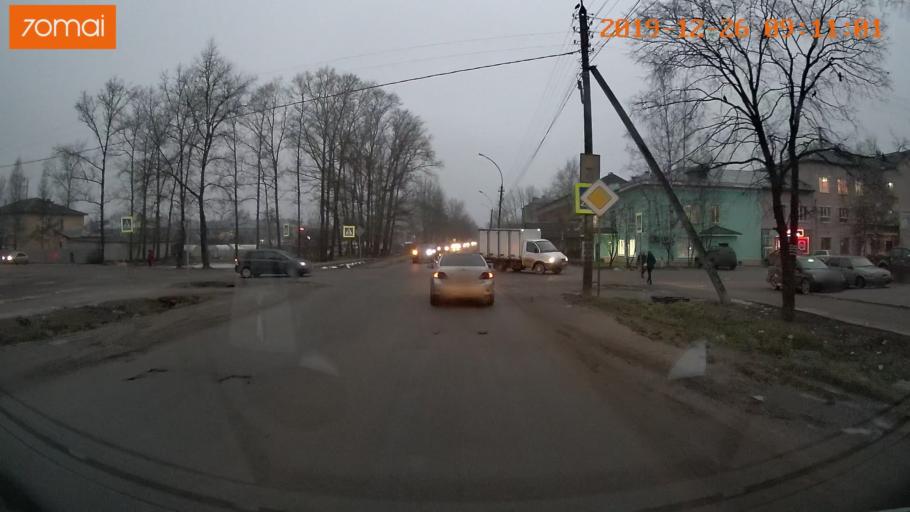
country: RU
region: Vologda
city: Gryazovets
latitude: 58.8740
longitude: 40.2525
